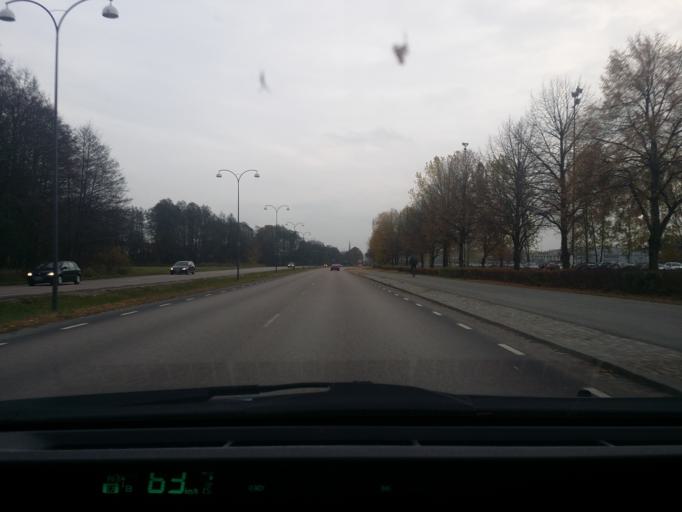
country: SE
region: Vaestmanland
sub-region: Vasteras
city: Vasteras
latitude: 59.6316
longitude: 16.5322
